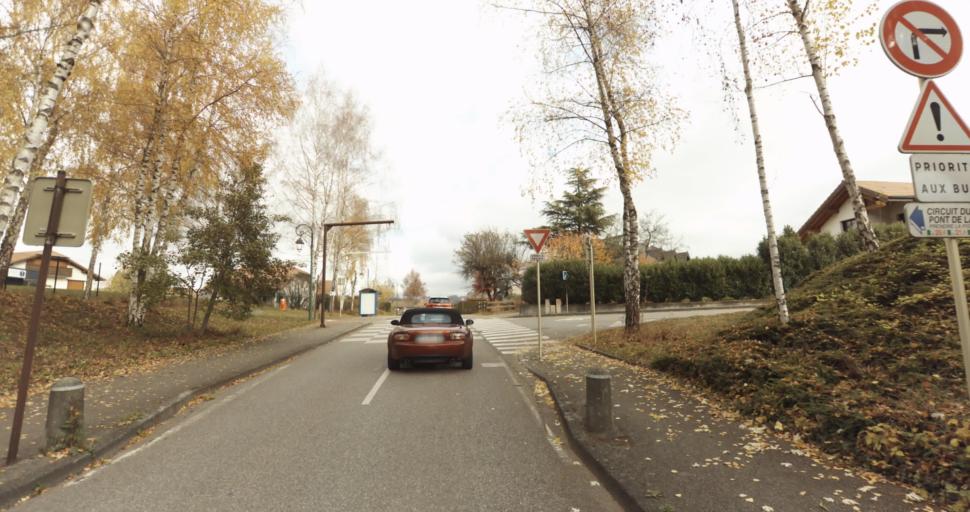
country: FR
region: Rhone-Alpes
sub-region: Departement de la Haute-Savoie
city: Metz-Tessy
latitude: 45.9354
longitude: 6.1098
